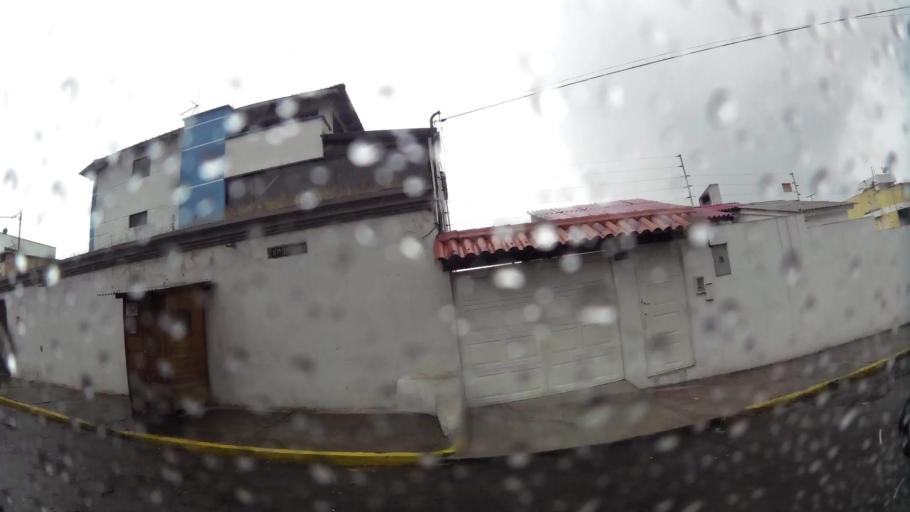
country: EC
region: Pichincha
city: Quito
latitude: -0.1064
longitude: -78.4981
